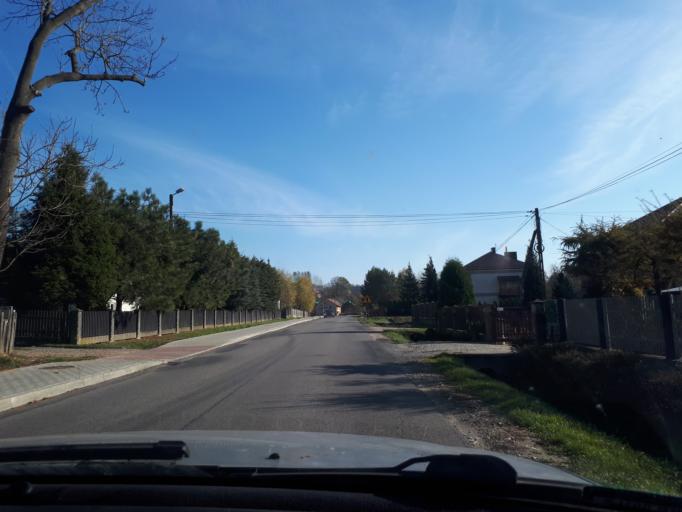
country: PL
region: Subcarpathian Voivodeship
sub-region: Powiat debicki
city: Debica
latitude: 50.0030
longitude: 21.4077
